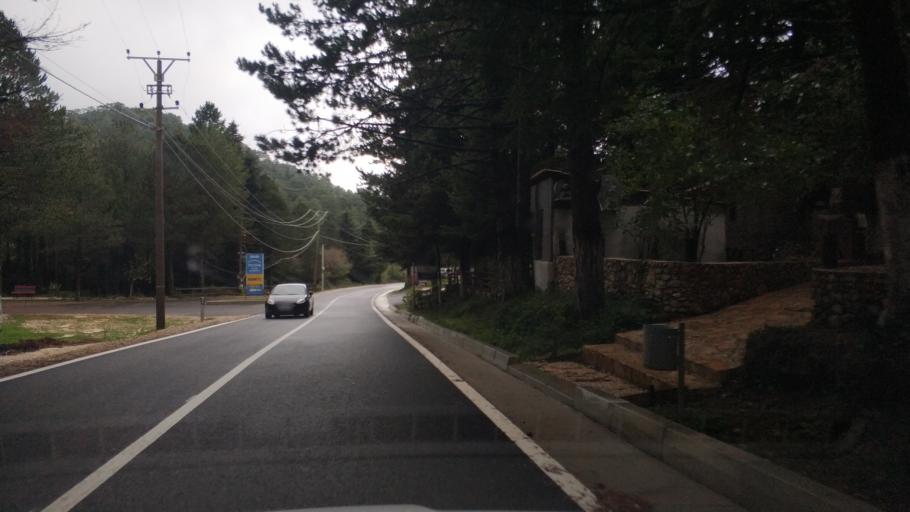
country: AL
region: Vlore
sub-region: Rrethi i Vlores
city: Brataj
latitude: 40.2098
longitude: 19.5797
